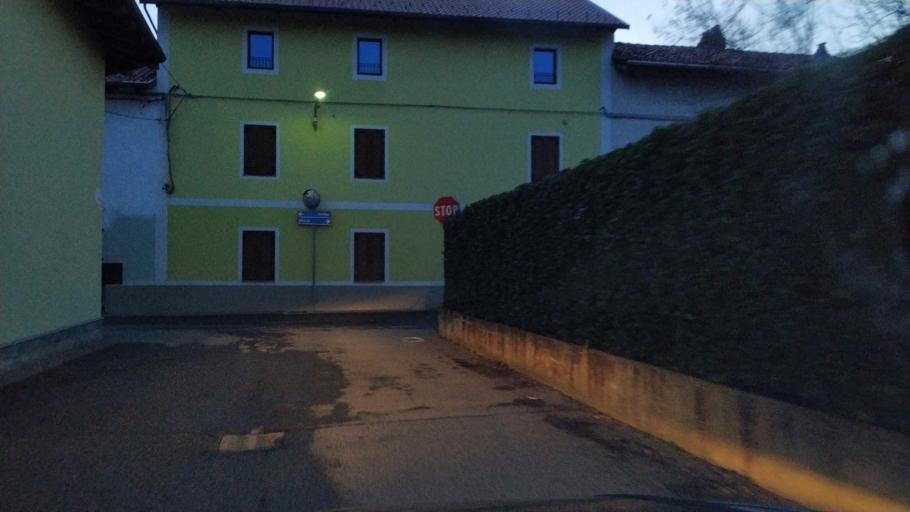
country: IT
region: Piedmont
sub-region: Provincia di Vercelli
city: Borgo d'Ale
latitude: 45.3482
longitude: 8.0481
